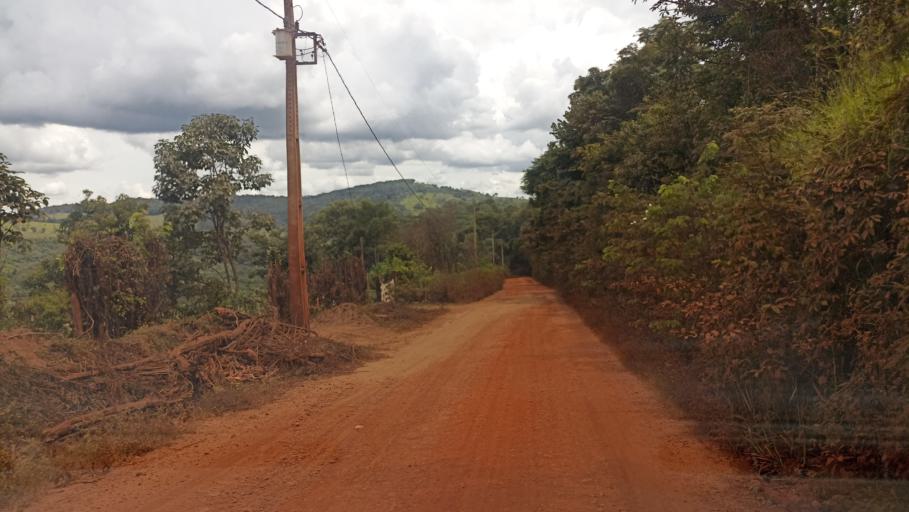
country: BR
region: Minas Gerais
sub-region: Itabirito
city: Itabirito
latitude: -20.3380
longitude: -43.7588
